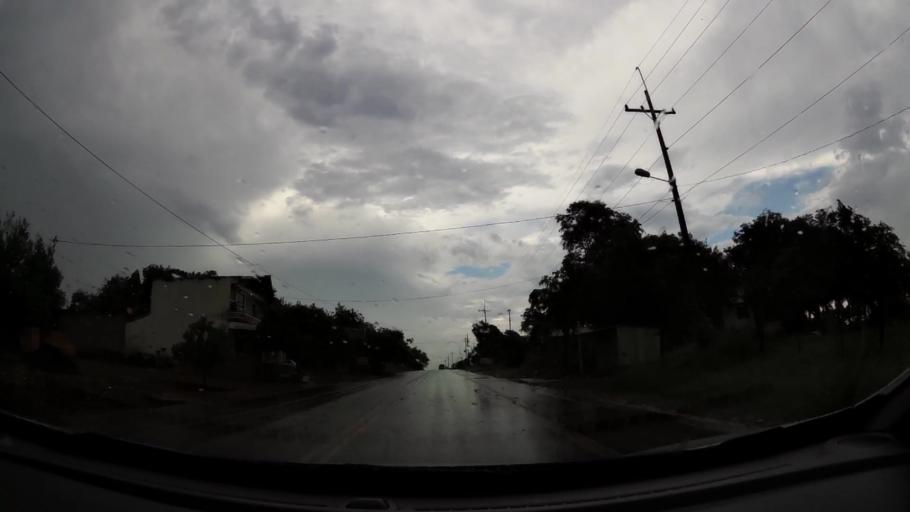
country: PY
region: Alto Parana
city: Presidente Franco
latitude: -25.5659
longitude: -54.6680
